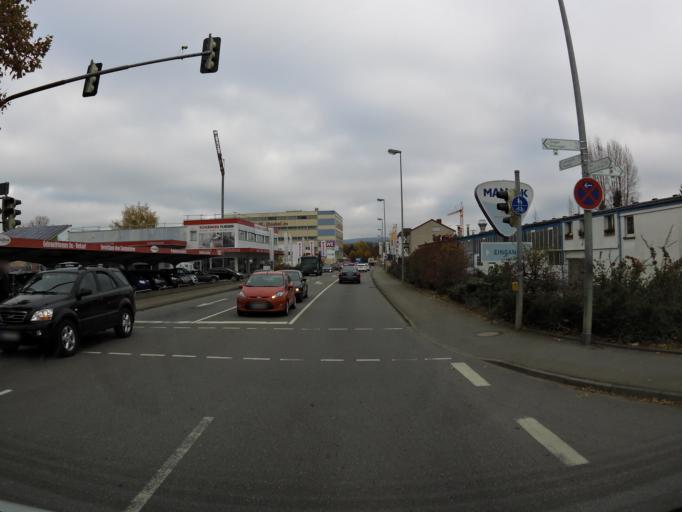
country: DE
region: Baden-Wuerttemberg
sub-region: Freiburg Region
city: Radolfzell am Bodensee
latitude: 47.7428
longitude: 8.9570
